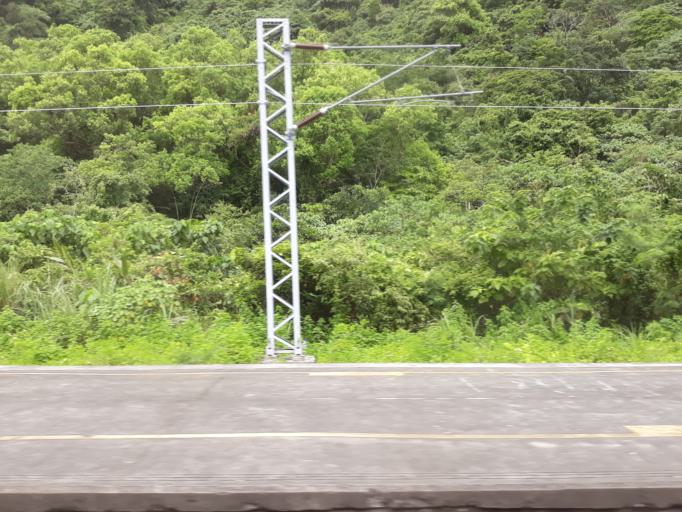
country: TW
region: Taiwan
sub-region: Yilan
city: Yilan
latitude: 24.4494
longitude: 121.7757
